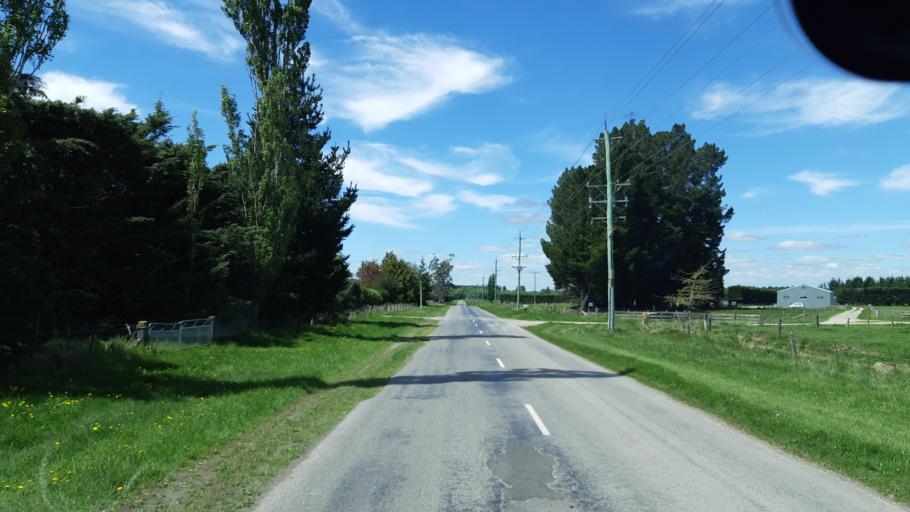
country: NZ
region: Canterbury
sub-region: Ashburton District
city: Methven
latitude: -43.7305
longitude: 171.5159
